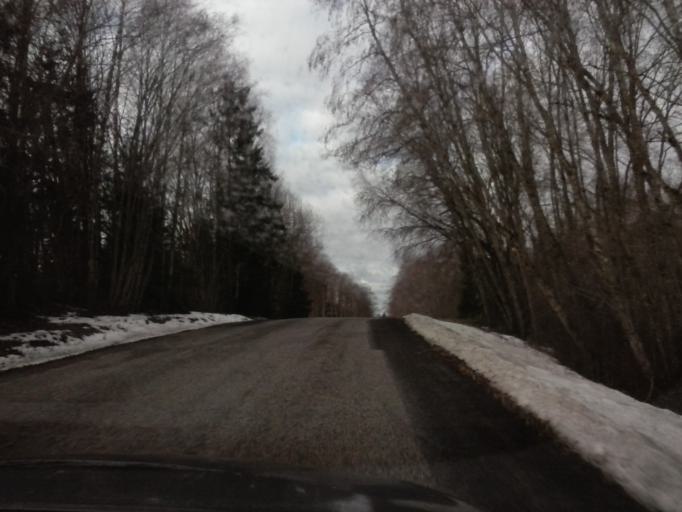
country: EE
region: Tartu
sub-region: Elva linn
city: Elva
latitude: 58.0040
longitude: 26.2859
